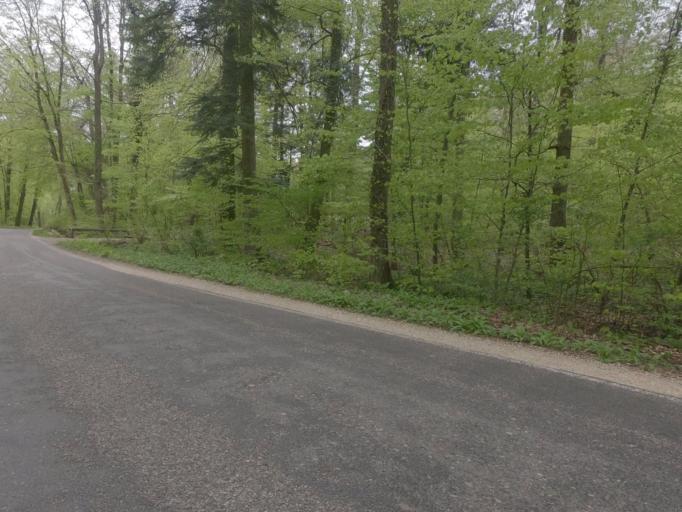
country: CH
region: Solothurn
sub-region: Bezirk Lebern
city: Riedholz
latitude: 47.2291
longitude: 7.5521
